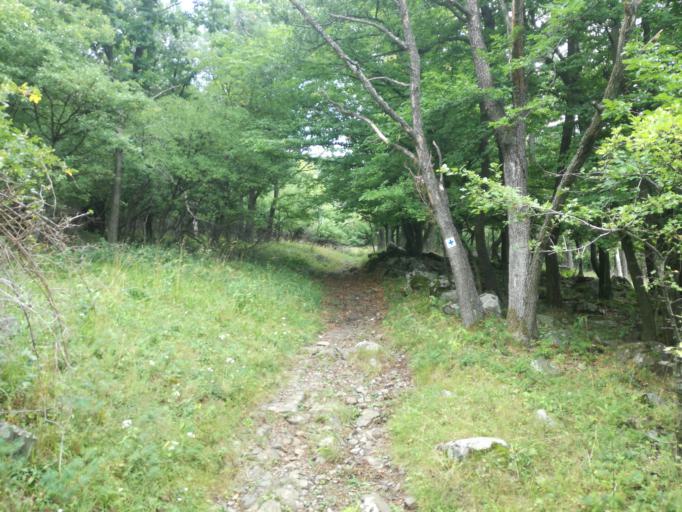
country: HU
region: Heves
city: Paradsasvar
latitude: 47.8582
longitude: 19.9889
